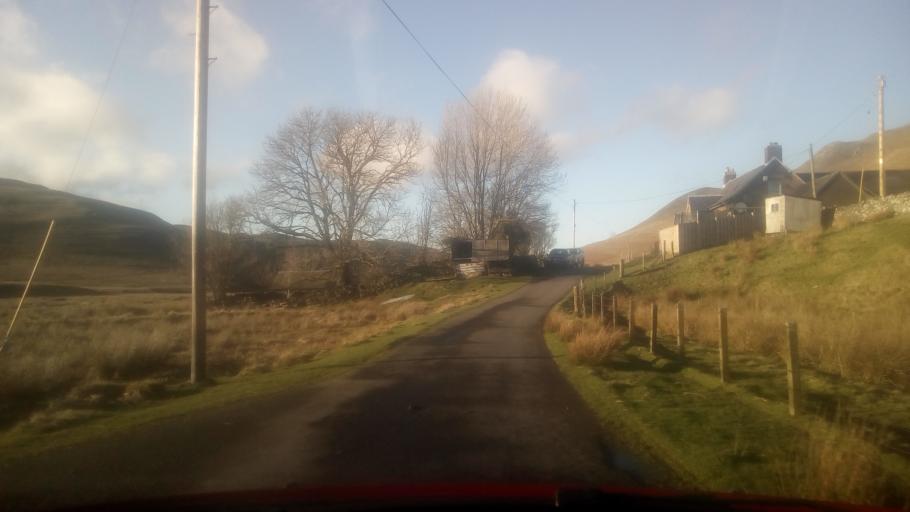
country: GB
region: England
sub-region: Northumberland
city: Rochester
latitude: 55.3883
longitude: -2.3744
